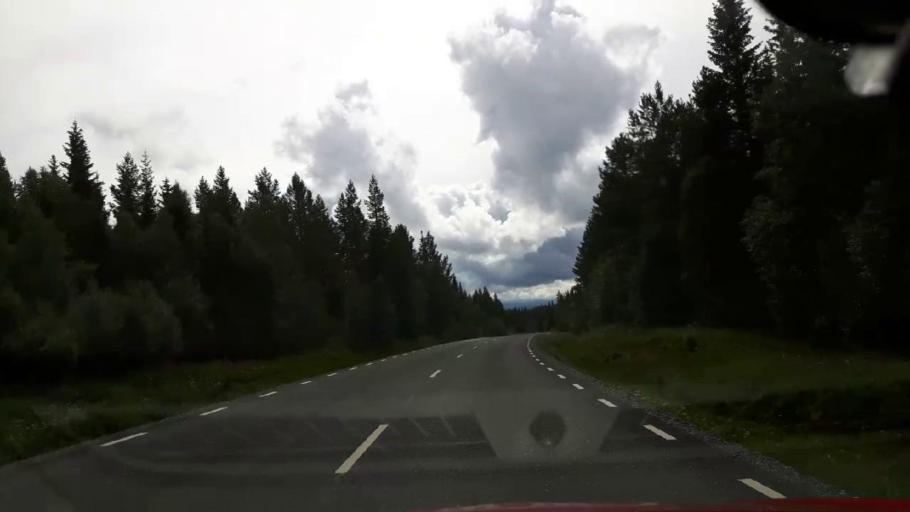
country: NO
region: Nord-Trondelag
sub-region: Lierne
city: Sandvika
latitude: 64.6227
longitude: 14.1222
